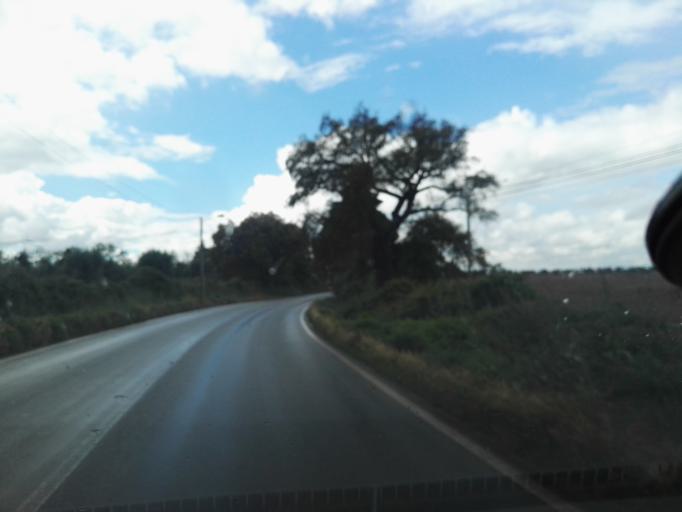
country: PT
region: Santarem
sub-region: Golega
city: Golega
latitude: 39.4152
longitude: -8.4944
